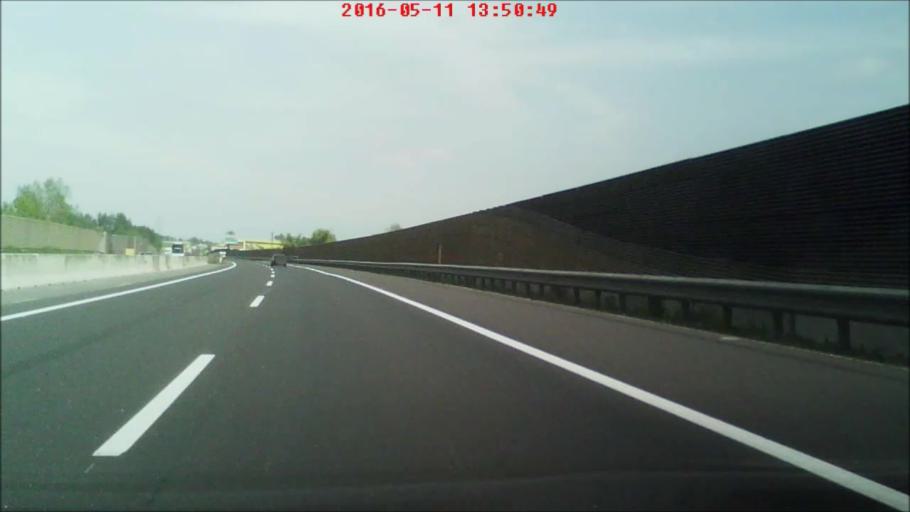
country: AT
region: Upper Austria
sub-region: Politischer Bezirk Vocklabruck
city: Wolfsegg am Hausruck
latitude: 48.1750
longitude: 13.7092
